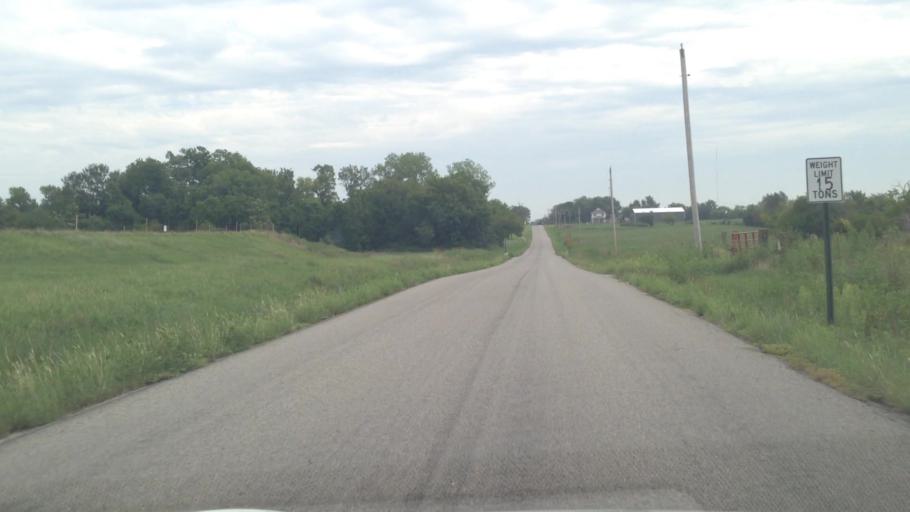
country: US
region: Kansas
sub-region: Crawford County
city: Girard
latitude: 37.4994
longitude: -94.8586
